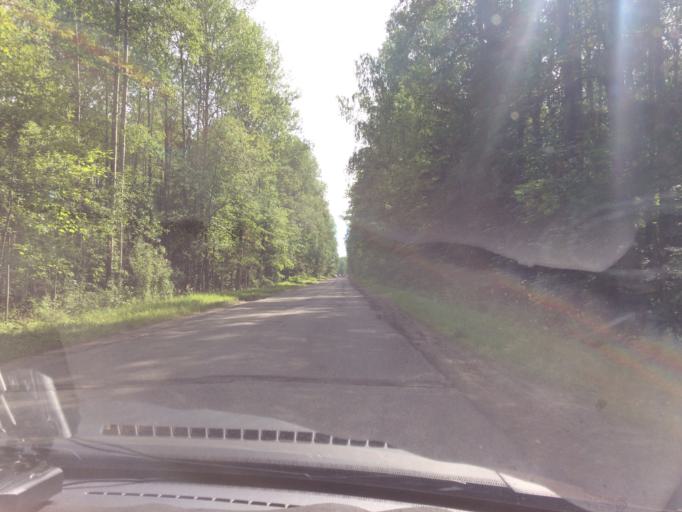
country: RU
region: Mariy-El
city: Surok
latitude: 56.5709
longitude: 48.1499
